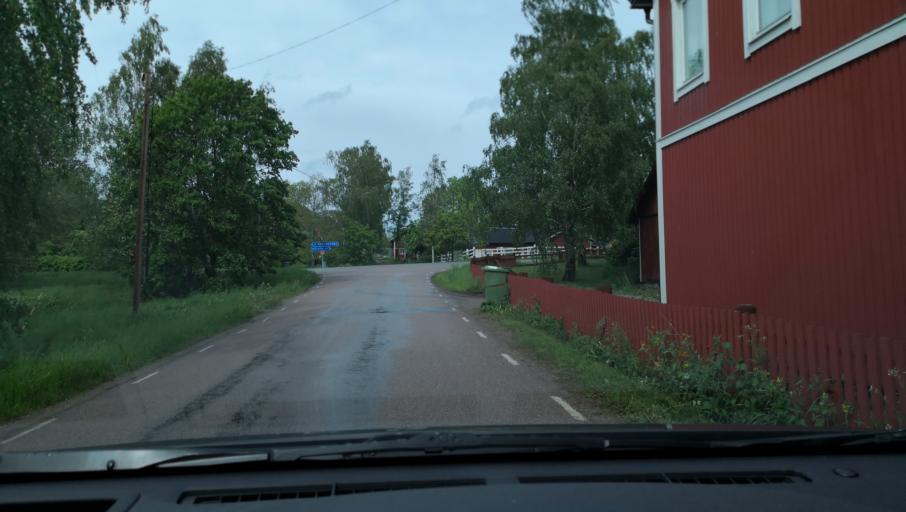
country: SE
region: Uppsala
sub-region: Enkopings Kommun
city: Orsundsbro
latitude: 59.6880
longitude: 17.3799
